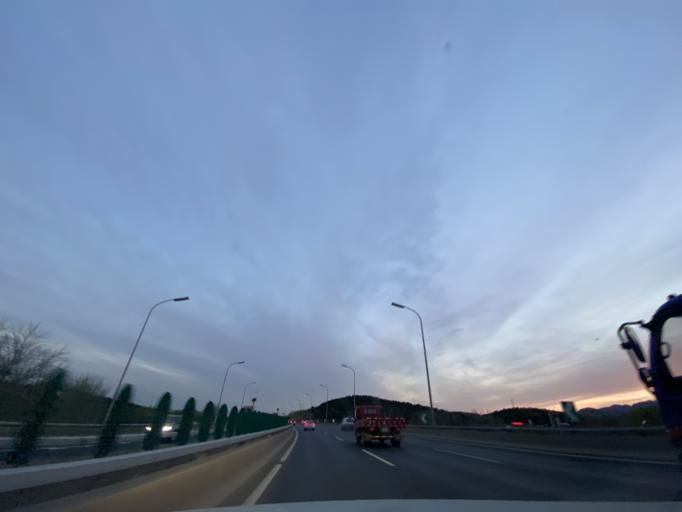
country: CN
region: Beijing
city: Haidian
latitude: 40.0087
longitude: 116.2663
